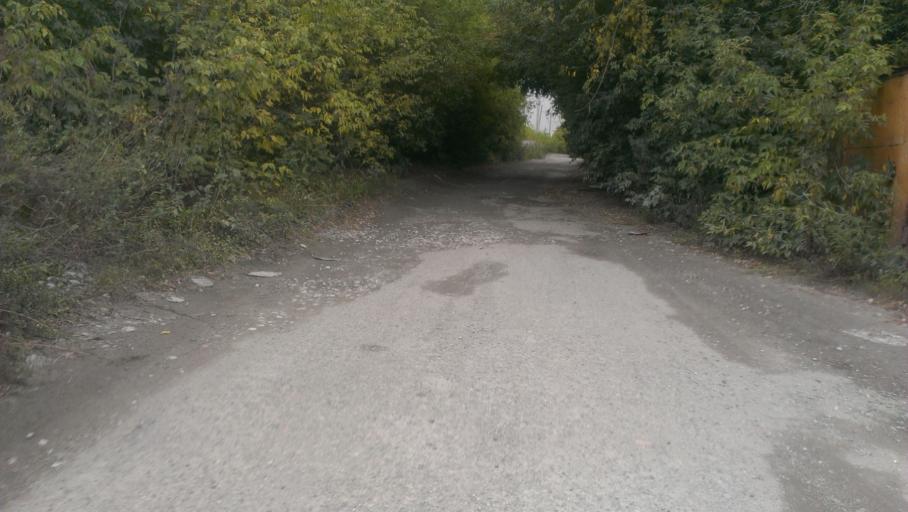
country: RU
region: Altai Krai
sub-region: Gorod Barnaulskiy
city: Barnaul
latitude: 53.3489
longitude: 83.7520
